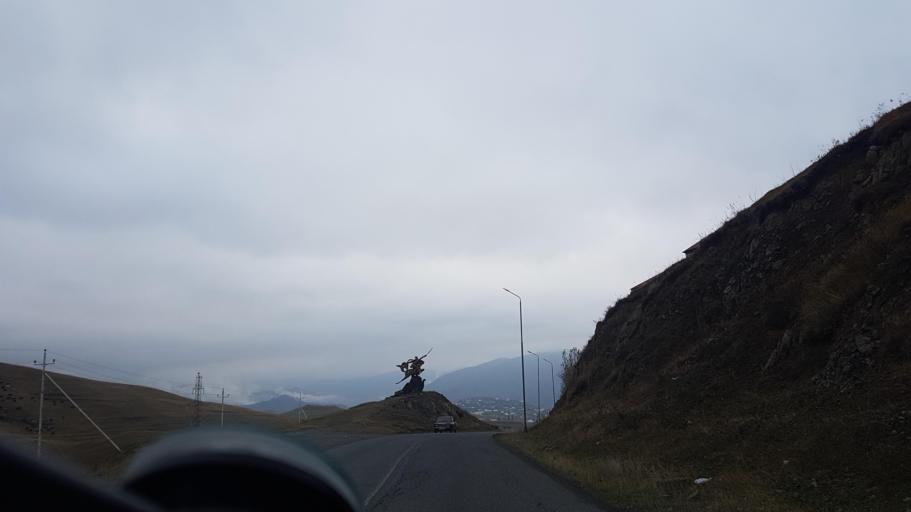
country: AZ
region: Gadabay Rayon
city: Ariqdam
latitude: 40.6144
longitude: 45.8113
